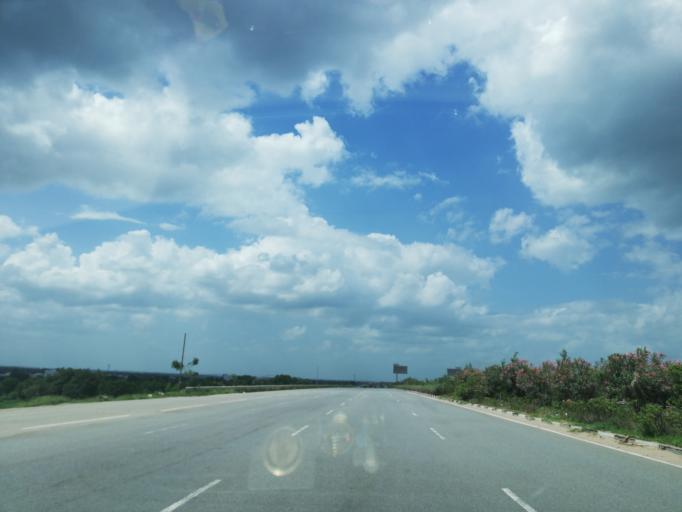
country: IN
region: Telangana
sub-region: Medak
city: Serilingampalle
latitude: 17.4689
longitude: 78.2486
